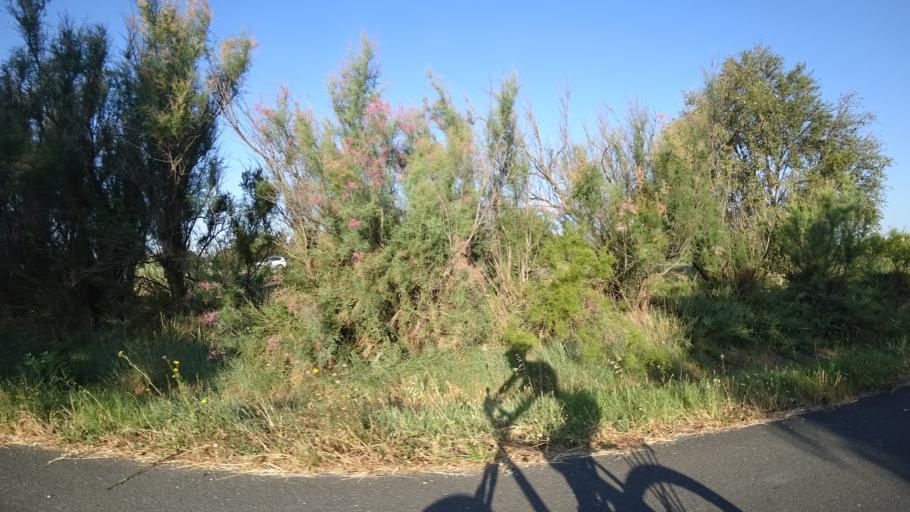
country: FR
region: Languedoc-Roussillon
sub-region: Departement des Pyrenees-Orientales
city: Sainte-Marie-Plage
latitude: 42.7343
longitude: 3.0259
